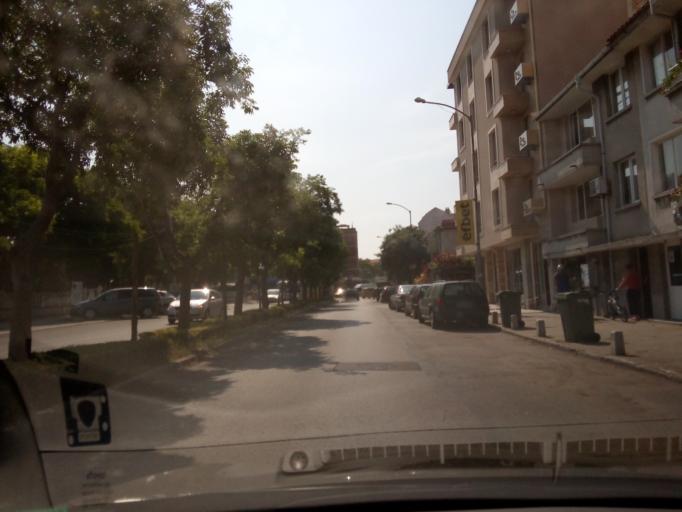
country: BG
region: Burgas
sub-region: Obshtina Pomorie
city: Pomorie
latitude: 42.5601
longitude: 27.6371
